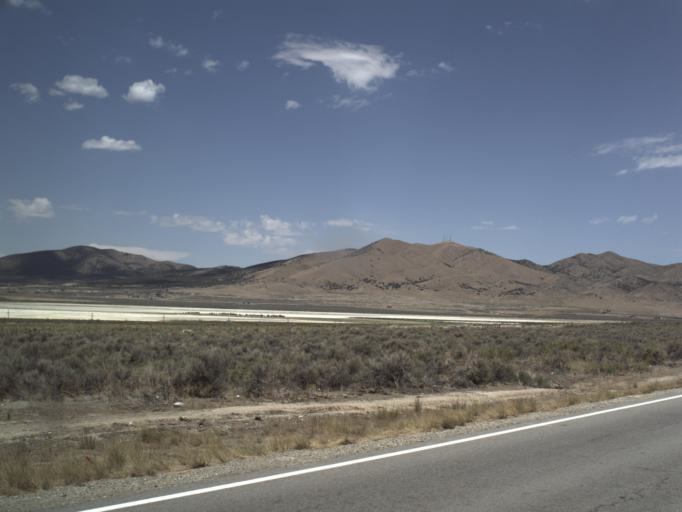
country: US
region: Utah
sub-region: Tooele County
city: Tooele
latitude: 40.4061
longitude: -112.3855
